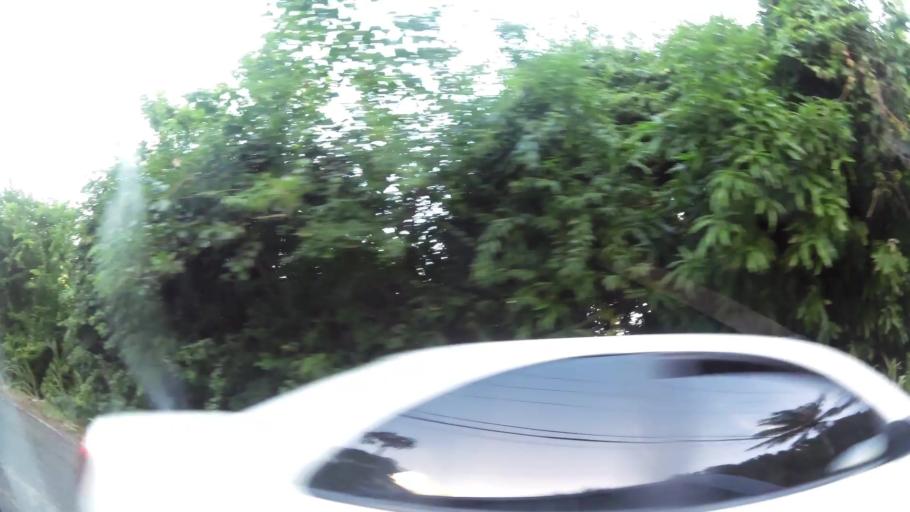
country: LC
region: Gros-Islet
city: Gros Islet
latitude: 14.0765
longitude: -60.9433
